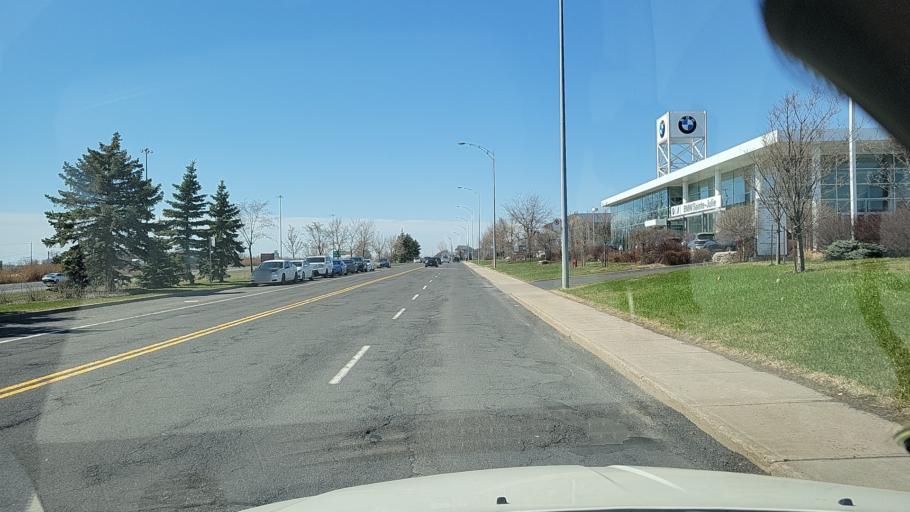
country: CA
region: Quebec
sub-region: Monteregie
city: Sainte-Julie
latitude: 45.5791
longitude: -73.3396
